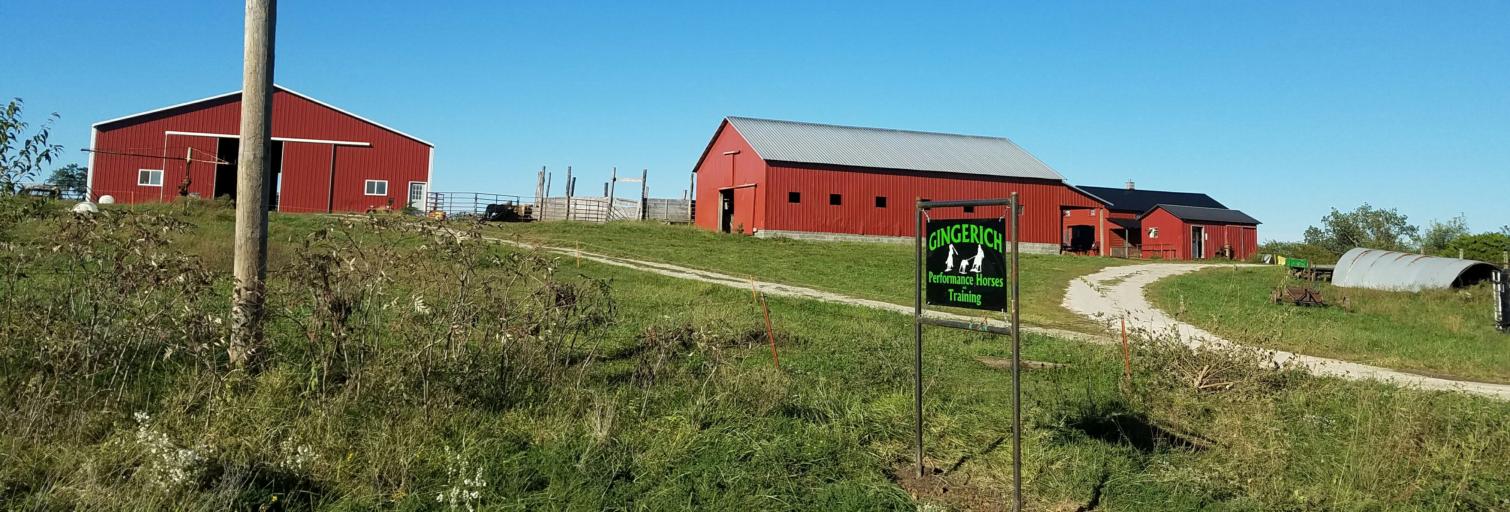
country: US
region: Iowa
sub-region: Decatur County
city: Lamoni
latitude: 40.6382
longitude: -93.8852
